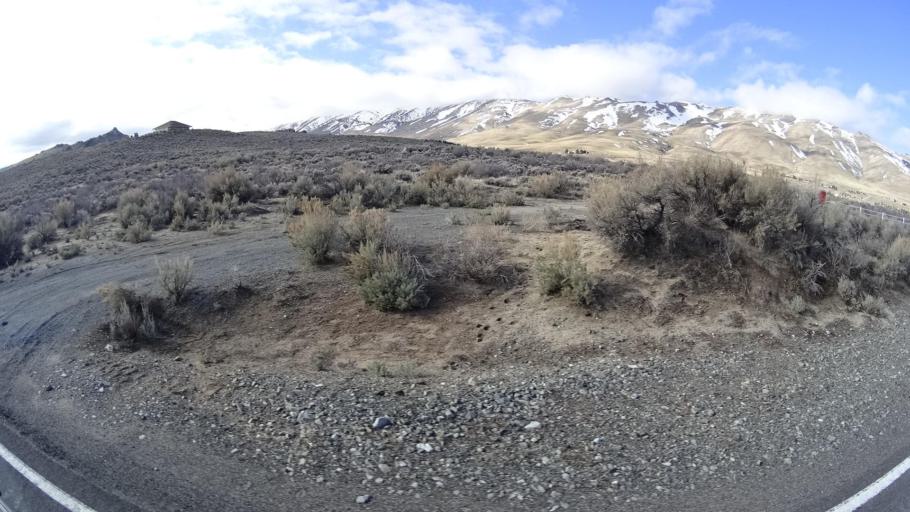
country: US
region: Nevada
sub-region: Washoe County
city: Cold Springs
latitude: 39.8678
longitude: -119.9503
